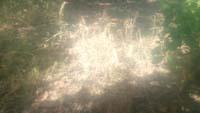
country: ML
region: Bamako
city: Bamako
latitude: 12.5915
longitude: -8.1002
